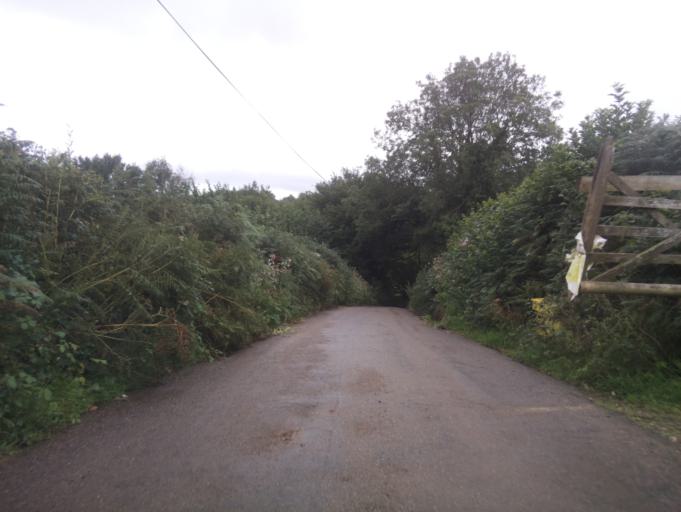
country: GB
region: England
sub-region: Devon
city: Totnes
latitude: 50.3392
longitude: -3.6849
